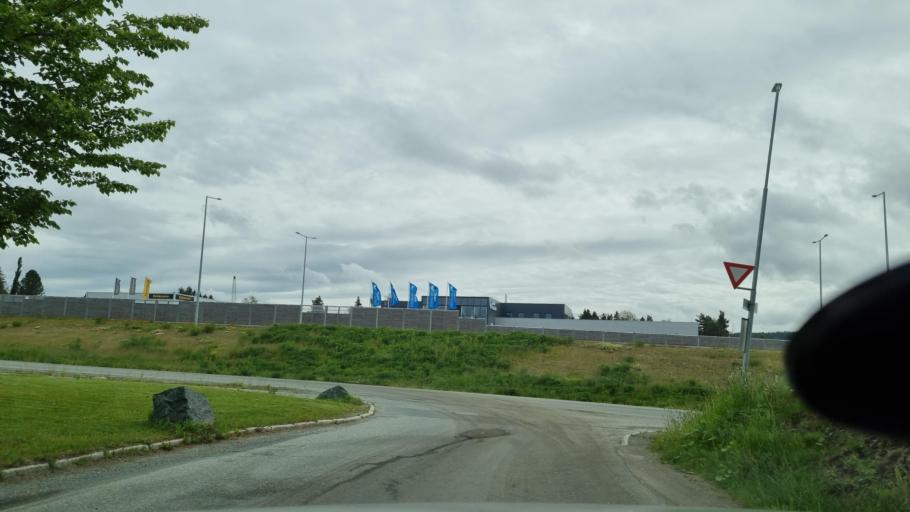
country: NO
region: Sor-Trondelag
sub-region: Melhus
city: Melhus
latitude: 63.3375
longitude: 10.3589
